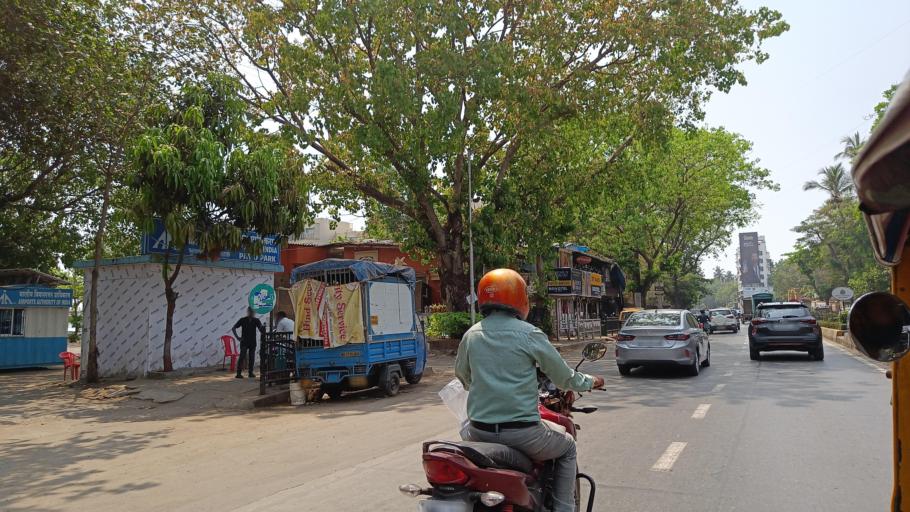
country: IN
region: Maharashtra
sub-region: Mumbai Suburban
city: Mumbai
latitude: 19.1037
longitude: 72.8269
